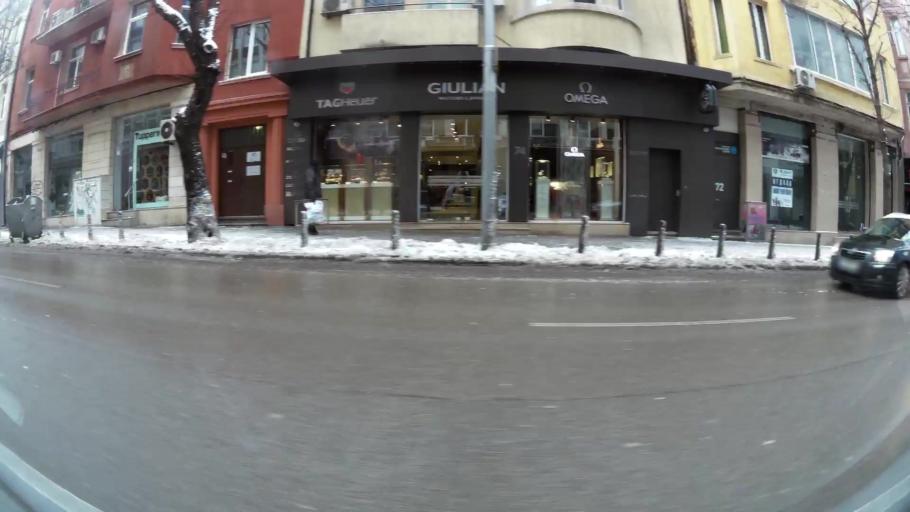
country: BG
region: Sofia-Capital
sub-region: Stolichna Obshtina
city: Sofia
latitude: 42.6992
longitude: 23.3296
